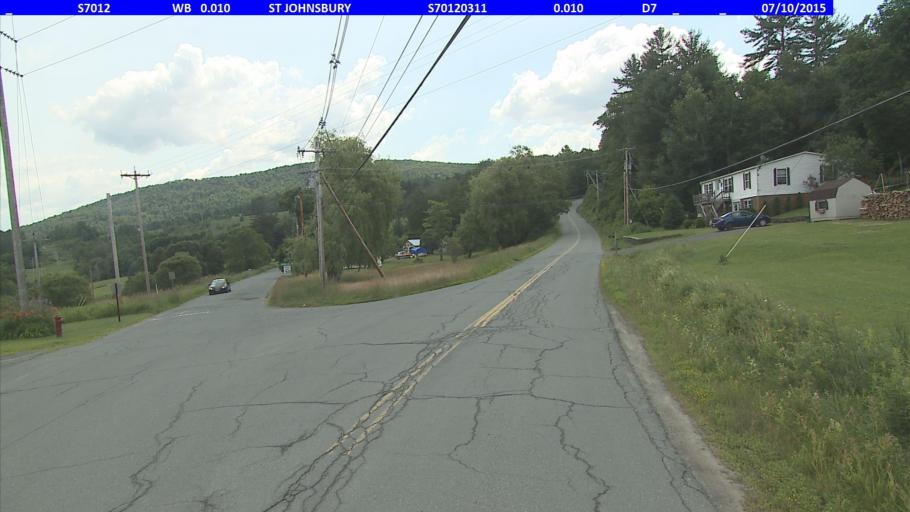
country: US
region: Vermont
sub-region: Caledonia County
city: Saint Johnsbury
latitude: 44.4169
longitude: -71.9921
